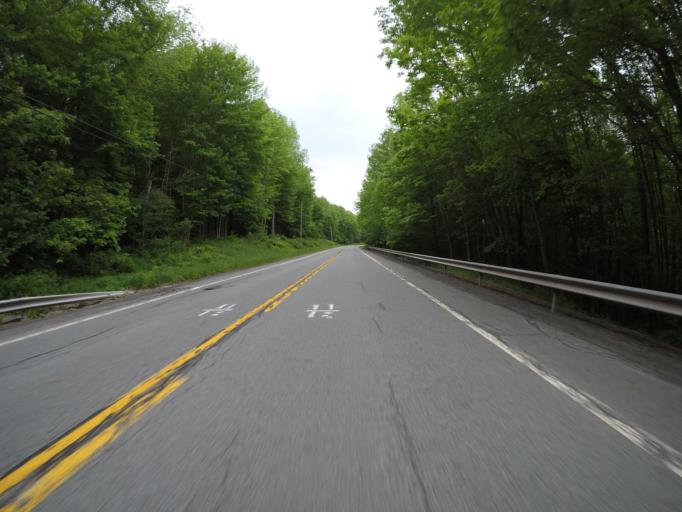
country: US
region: New York
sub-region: Sullivan County
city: Livingston Manor
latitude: 42.0696
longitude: -74.8847
